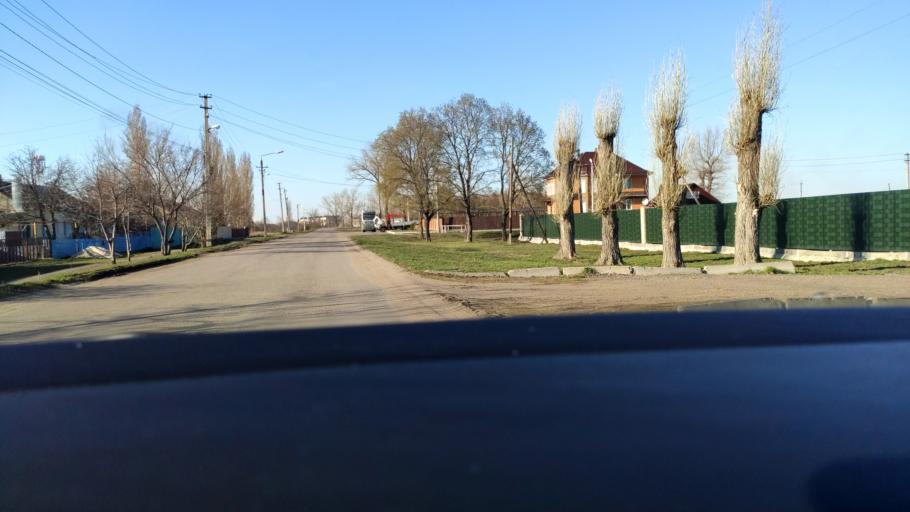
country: RU
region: Voronezj
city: Maslovka
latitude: 51.5069
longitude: 39.2943
